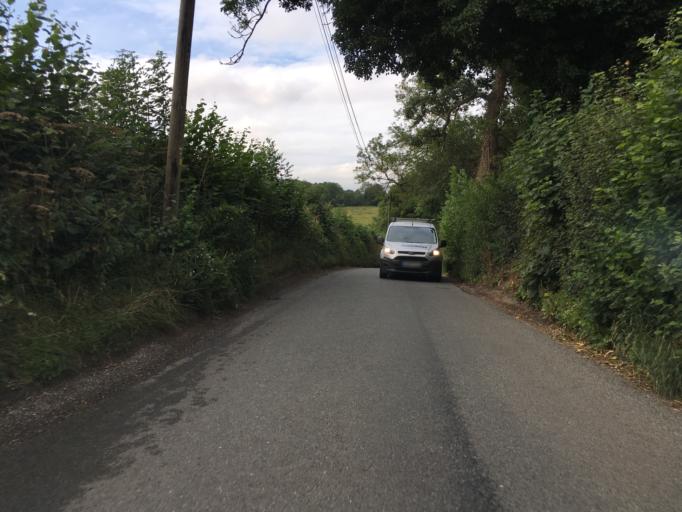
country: GB
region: England
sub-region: Hampshire
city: Colden Common
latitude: 50.9919
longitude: -1.2718
